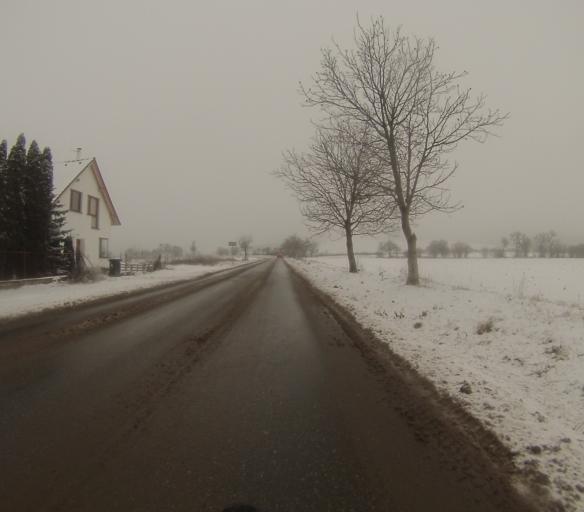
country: CZ
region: South Moravian
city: Ostopovice
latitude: 49.1623
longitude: 16.5289
